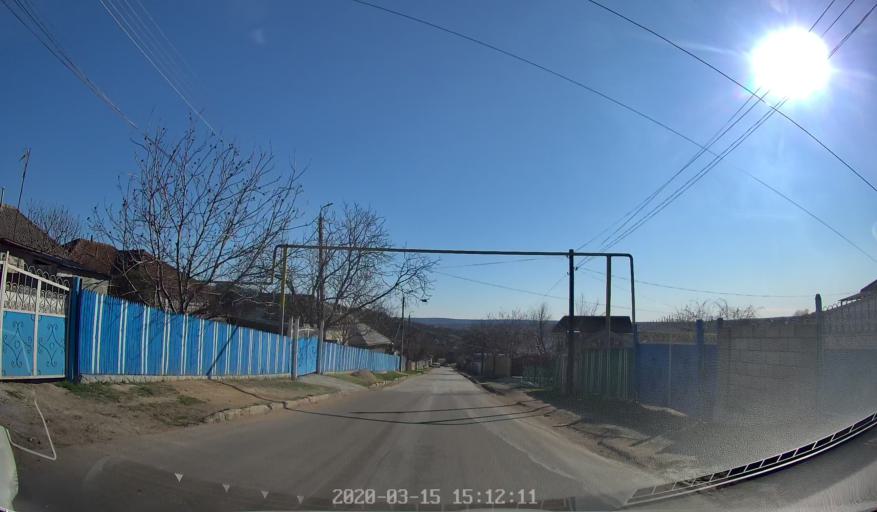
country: MD
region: Orhei
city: Orhei
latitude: 47.2573
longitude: 28.7742
